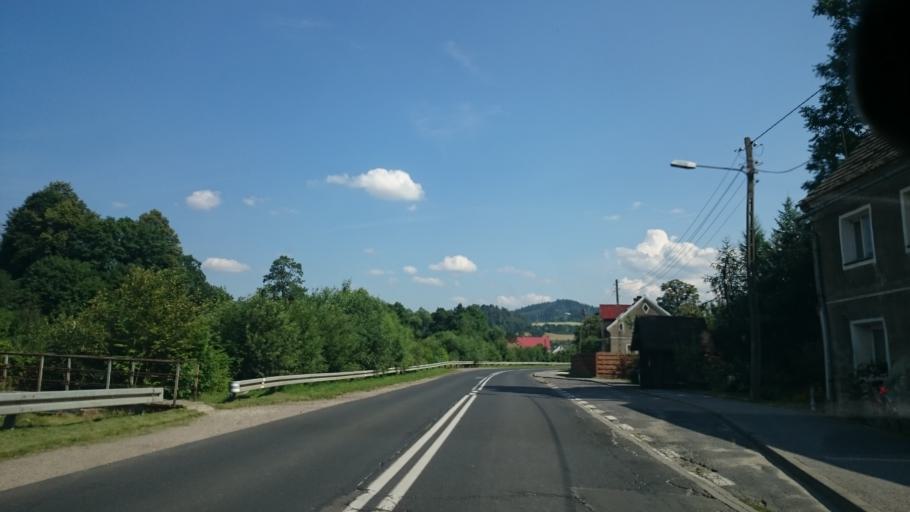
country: PL
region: Lower Silesian Voivodeship
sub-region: Powiat klodzki
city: Ladek-Zdroj
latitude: 50.3445
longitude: 16.7981
